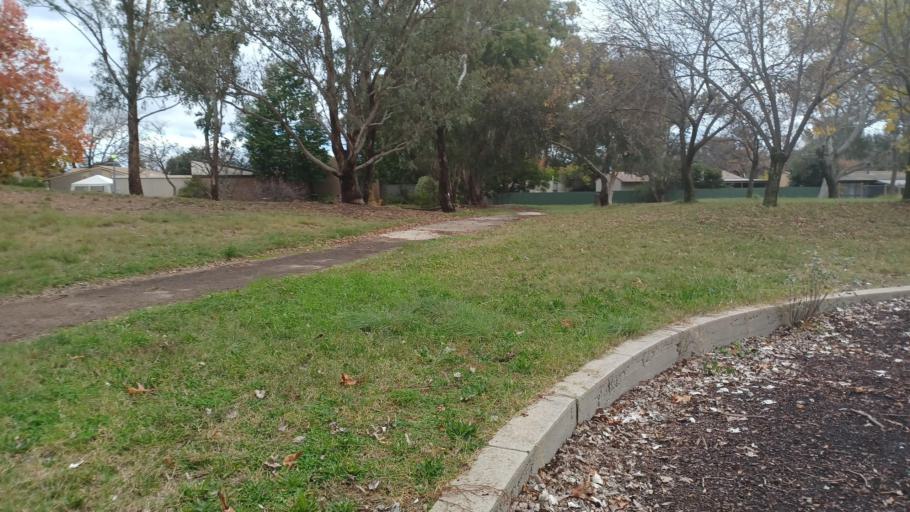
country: AU
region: Australian Capital Territory
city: Belconnen
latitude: -35.1999
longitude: 149.0418
